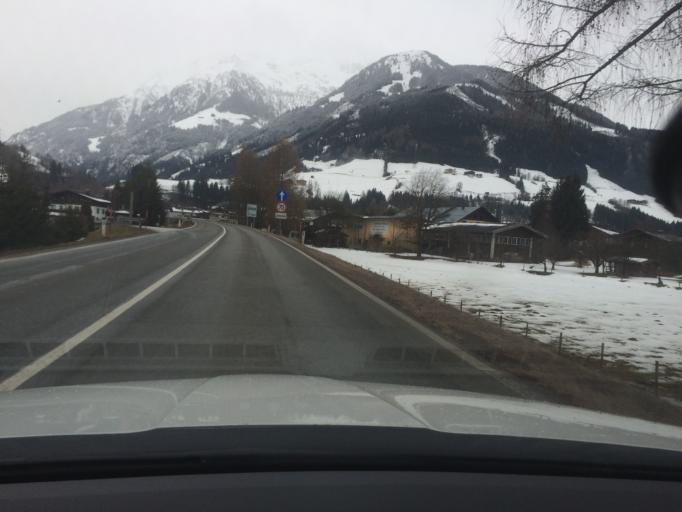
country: AT
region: Salzburg
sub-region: Politischer Bezirk Zell am See
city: Mittersill
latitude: 47.2794
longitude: 12.4886
